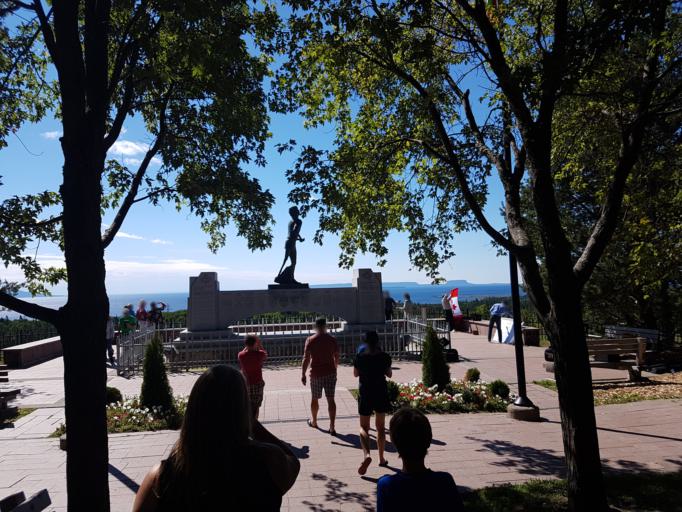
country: CA
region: Ontario
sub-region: Thunder Bay District
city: Thunder Bay
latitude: 48.4846
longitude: -89.1681
